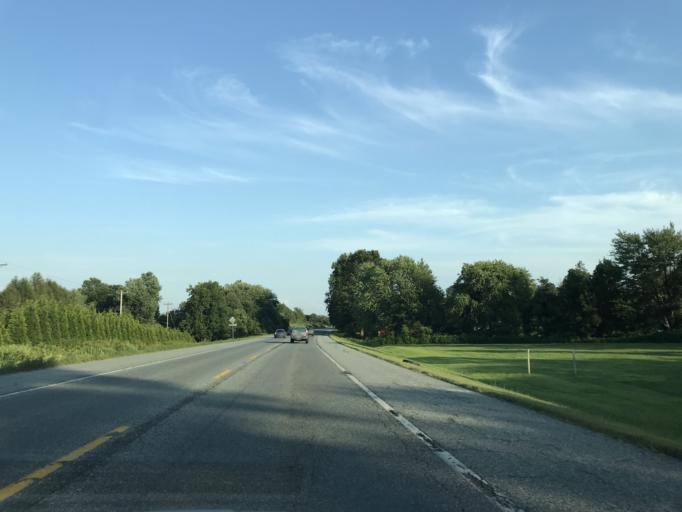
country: US
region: Maryland
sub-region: Cecil County
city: North East
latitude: 39.6806
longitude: -75.9677
